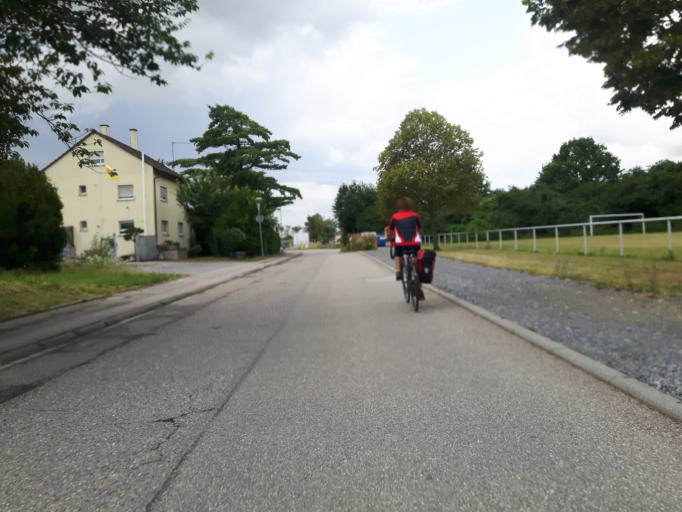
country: DE
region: Baden-Wuerttemberg
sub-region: Regierungsbezirk Stuttgart
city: Eppingen
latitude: 49.1313
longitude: 8.9238
